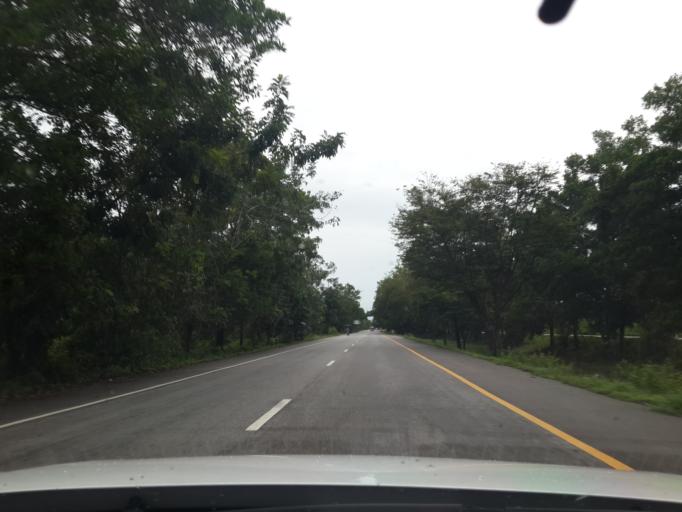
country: TH
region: Songkhla
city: Thepha
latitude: 6.8367
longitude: 101.0176
